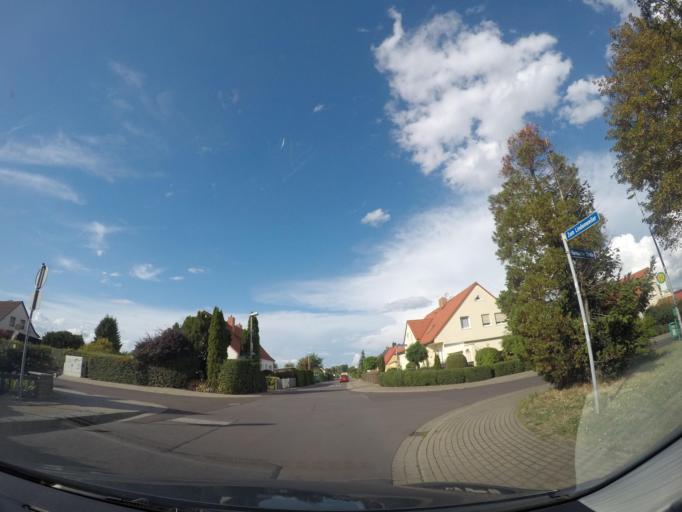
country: DE
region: Saxony-Anhalt
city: Diesdorf
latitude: 52.1356
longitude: 11.5801
